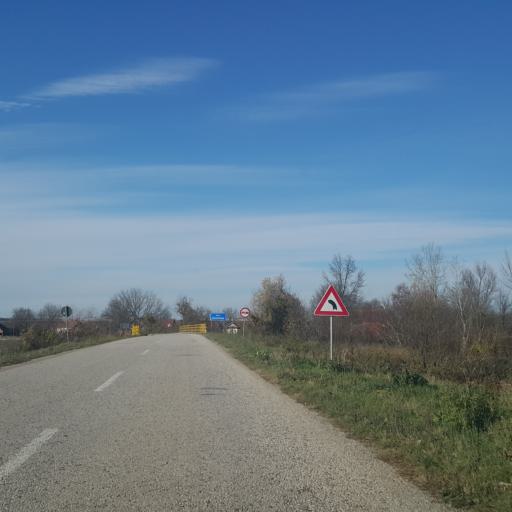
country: RS
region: Central Serbia
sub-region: Sumadijski Okrug
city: Topola
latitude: 44.2573
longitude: 20.8256
